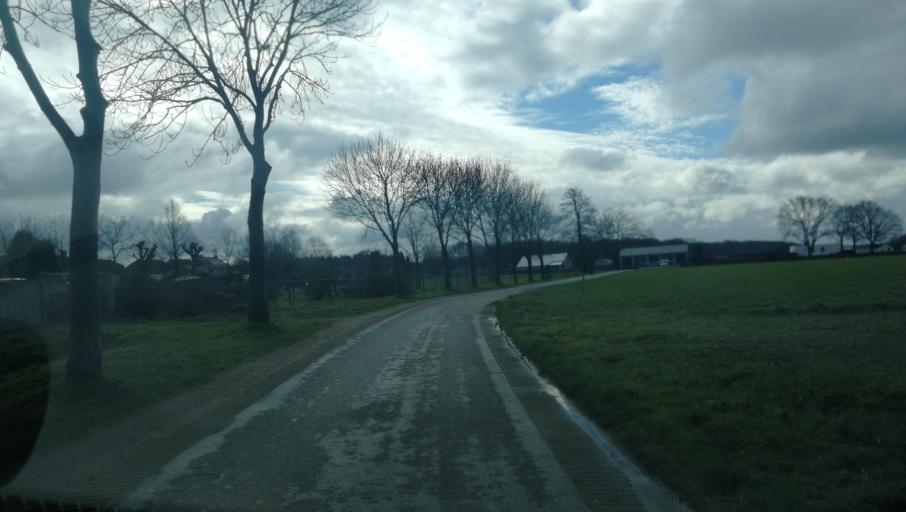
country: NL
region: Limburg
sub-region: Gemeente Venlo
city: Venlo
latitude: 51.4098
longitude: 6.1620
